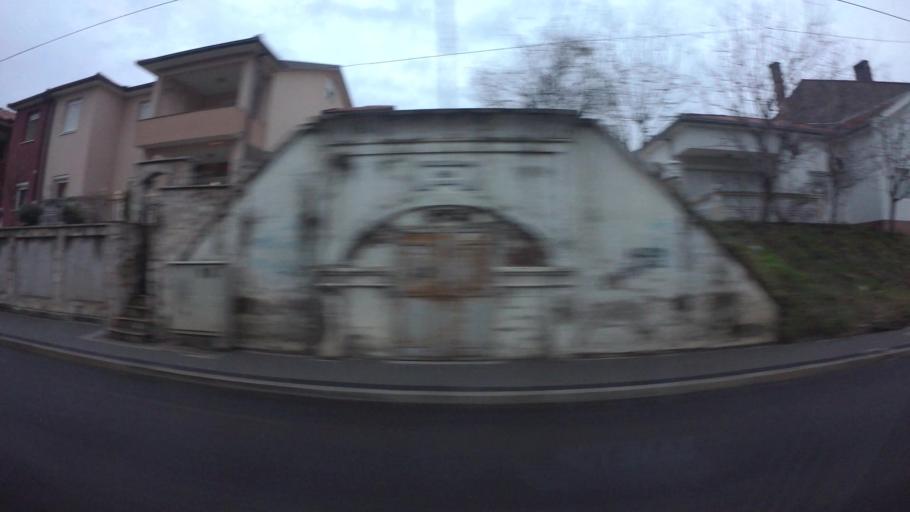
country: BA
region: Federation of Bosnia and Herzegovina
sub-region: Hercegovacko-Bosanski Kanton
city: Mostar
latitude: 43.3520
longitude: 17.8124
